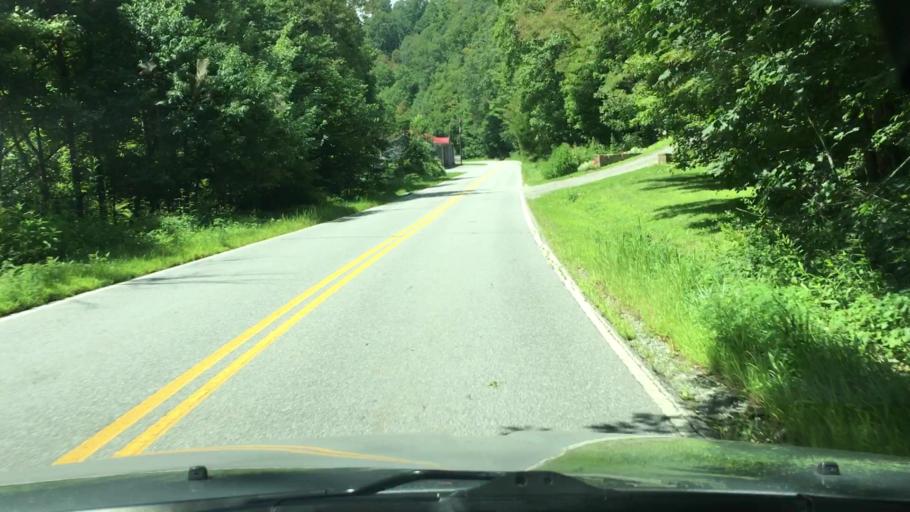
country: US
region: North Carolina
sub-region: Madison County
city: Mars Hill
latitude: 35.9181
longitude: -82.5437
